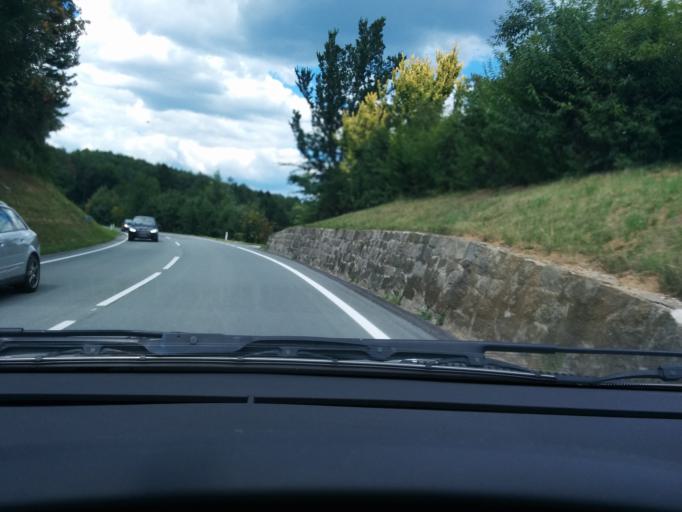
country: AT
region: Styria
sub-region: Politischer Bezirk Weiz
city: Nitscha
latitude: 47.1338
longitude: 15.7307
